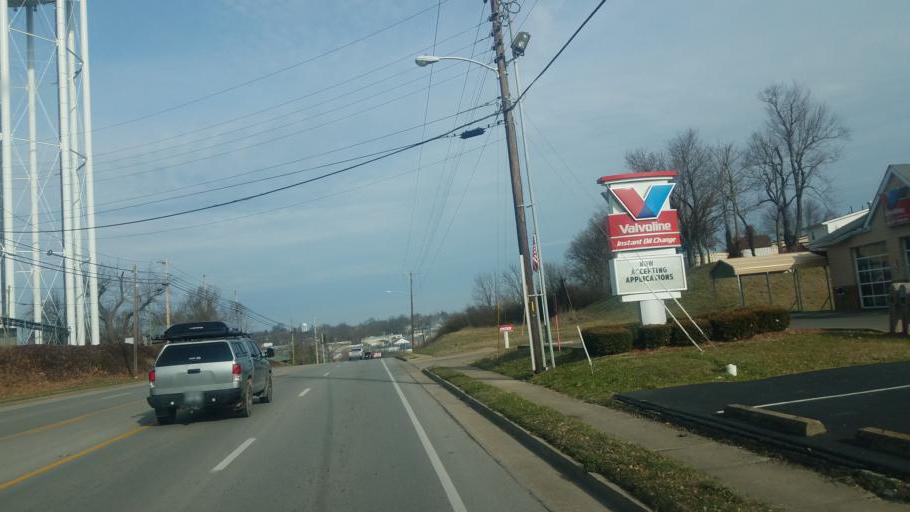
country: US
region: Kentucky
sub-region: Boyle County
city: Danville
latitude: 37.6326
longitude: -84.7750
